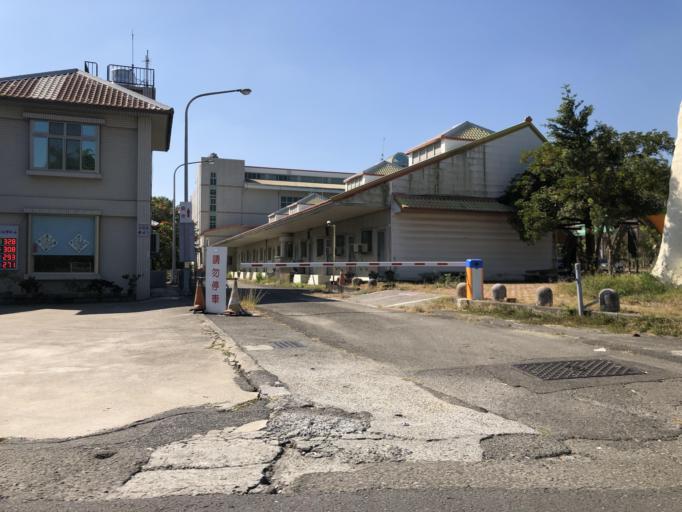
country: TW
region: Taiwan
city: Yujing
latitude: 23.0629
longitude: 120.3896
